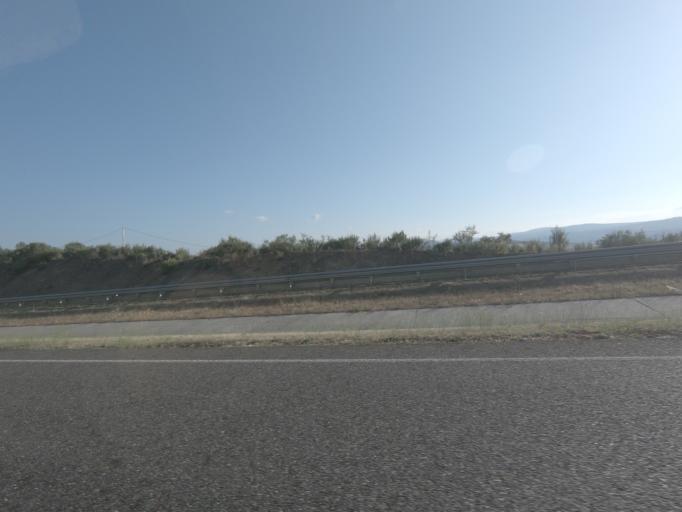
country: ES
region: Galicia
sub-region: Provincia de Ourense
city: Oimbra
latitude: 41.8511
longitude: -7.4138
